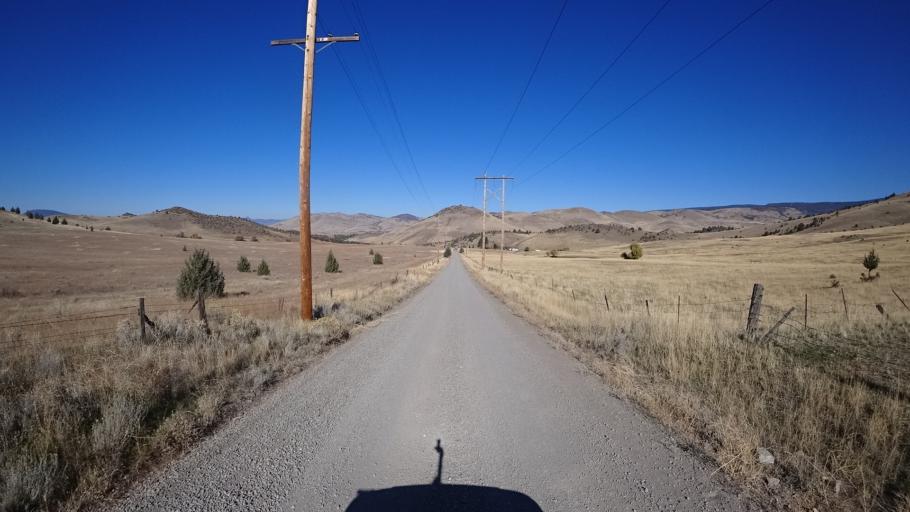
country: US
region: California
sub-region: Siskiyou County
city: Montague
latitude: 41.7789
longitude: -122.3591
